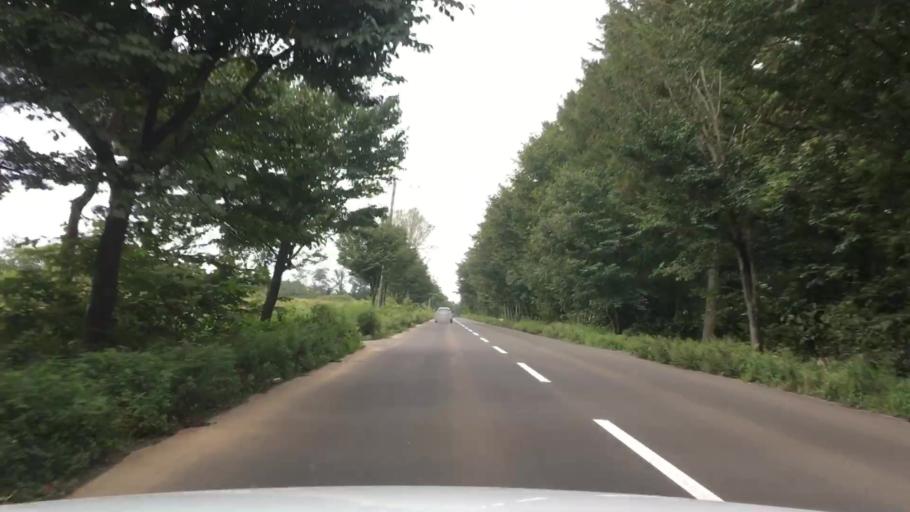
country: JP
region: Aomori
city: Shimokizukuri
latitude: 40.7155
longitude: 140.3162
